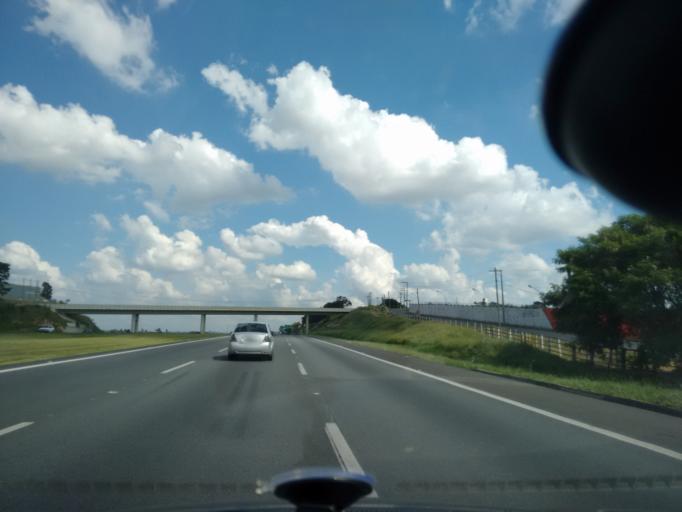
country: BR
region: Sao Paulo
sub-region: Campinas
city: Campinas
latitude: -22.9855
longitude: -47.1118
